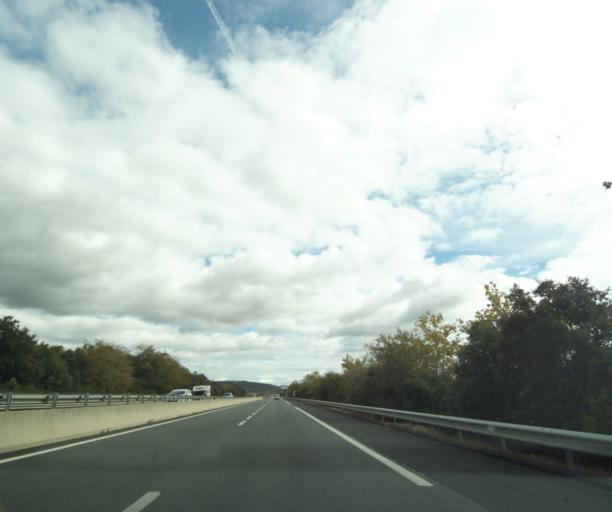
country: FR
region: Languedoc-Roussillon
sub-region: Departement de l'Herault
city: Nebian
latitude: 43.6787
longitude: 3.4020
